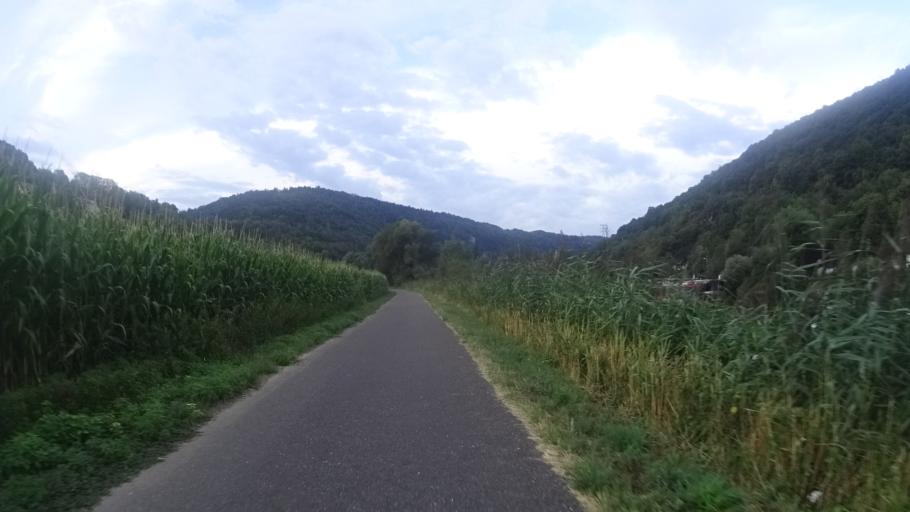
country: FR
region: Franche-Comte
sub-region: Departement du Doubs
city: Morre
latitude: 47.2375
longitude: 6.0621
